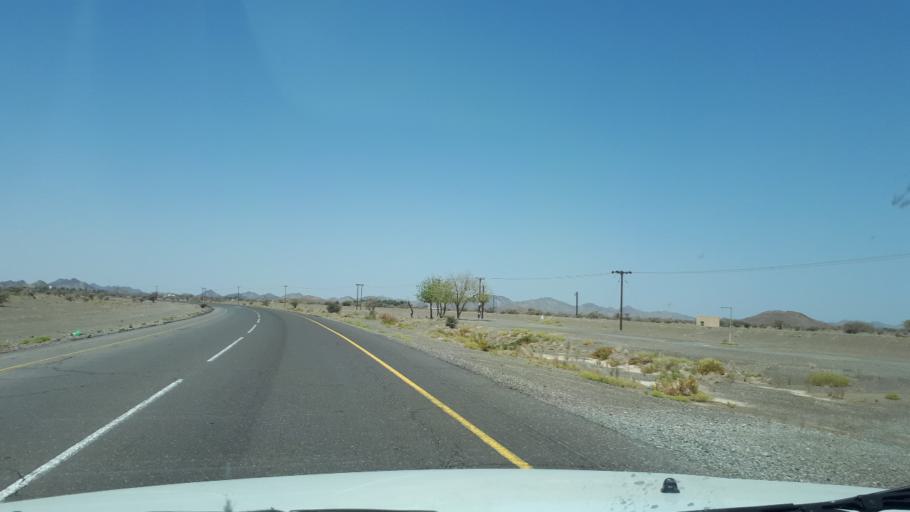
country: OM
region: Ash Sharqiyah
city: Ibra'
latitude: 22.6206
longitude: 58.4101
